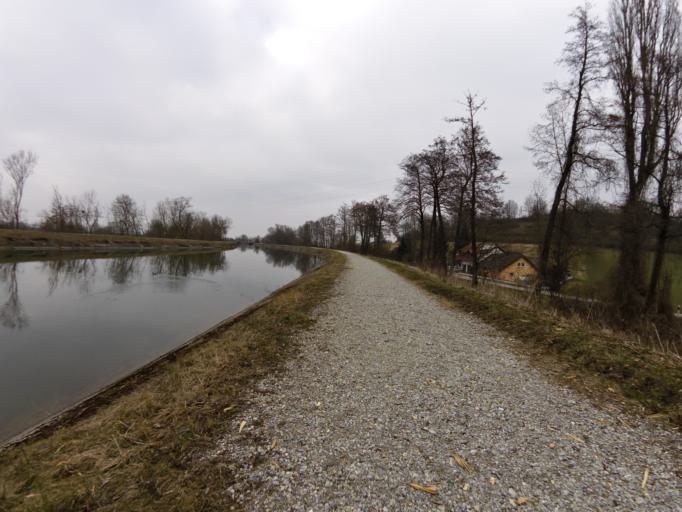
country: DE
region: Bavaria
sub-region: Upper Bavaria
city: Langenpreising
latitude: 48.4373
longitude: 11.9931
